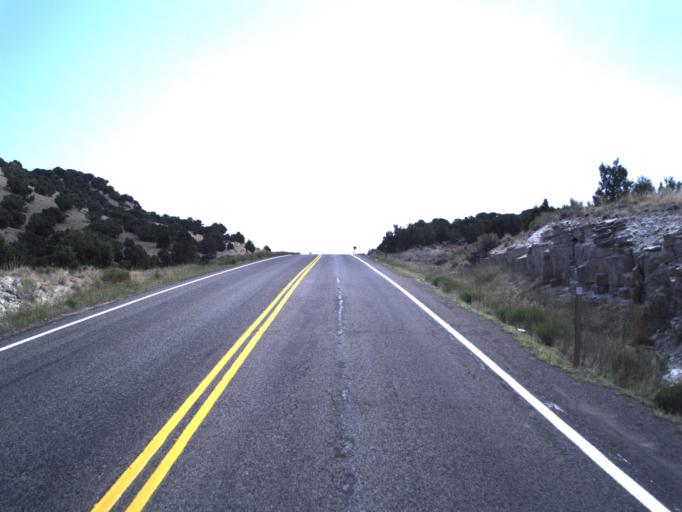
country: US
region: Utah
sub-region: Daggett County
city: Manila
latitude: 40.9385
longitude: -109.7092
